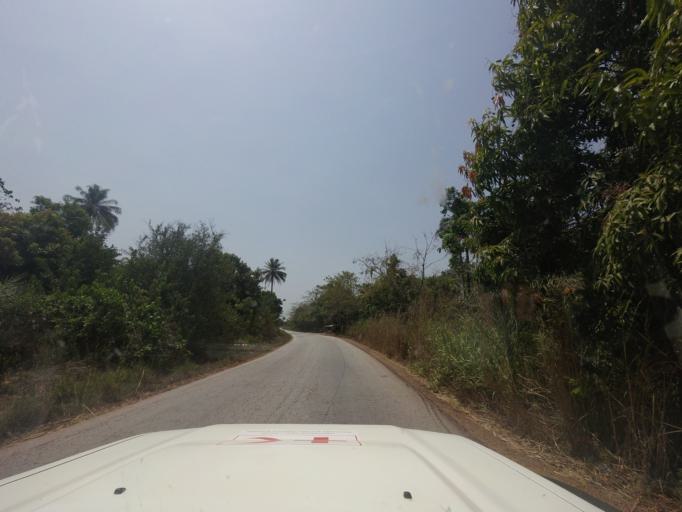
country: GN
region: Kindia
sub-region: Kindia
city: Kindia
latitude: 9.8812
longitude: -13.0547
